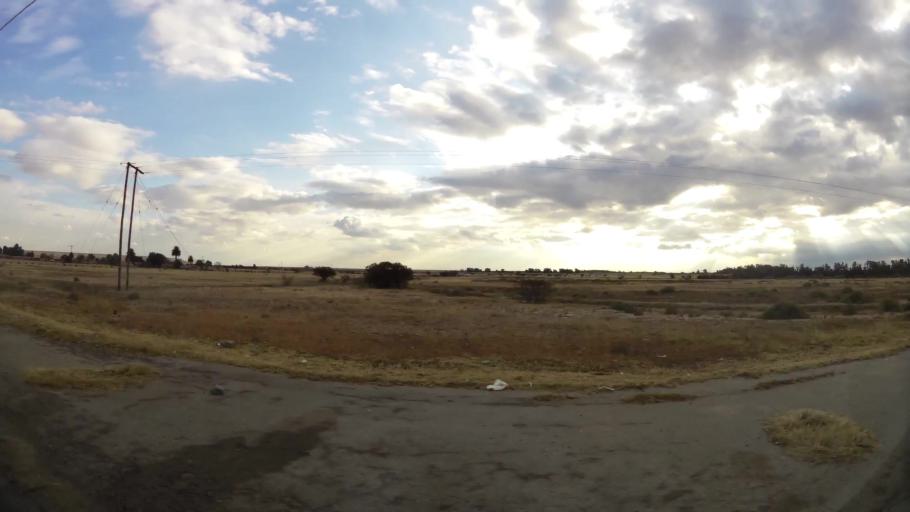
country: ZA
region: Orange Free State
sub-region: Lejweleputswa District Municipality
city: Welkom
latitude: -28.0089
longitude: 26.7099
